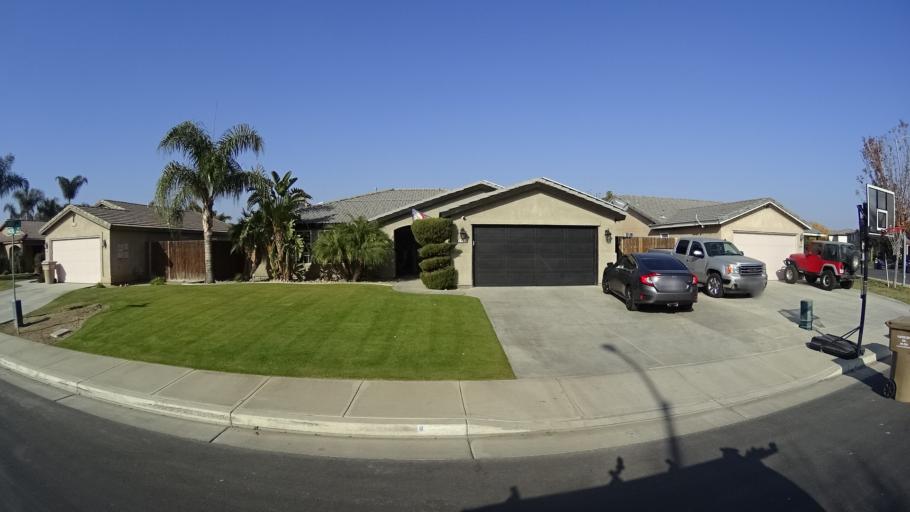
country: US
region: California
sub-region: Kern County
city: Greenacres
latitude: 35.3910
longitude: -119.0687
